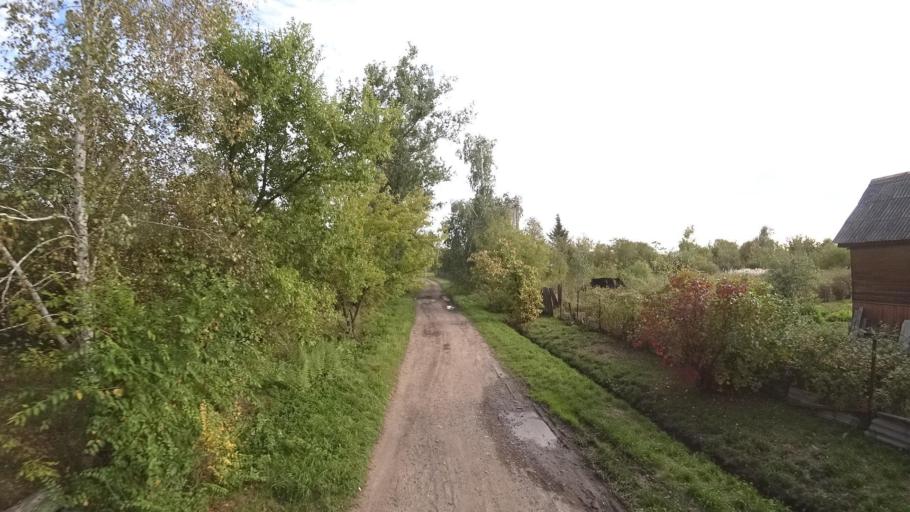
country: RU
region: Primorskiy
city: Dostoyevka
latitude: 44.2893
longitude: 133.4306
